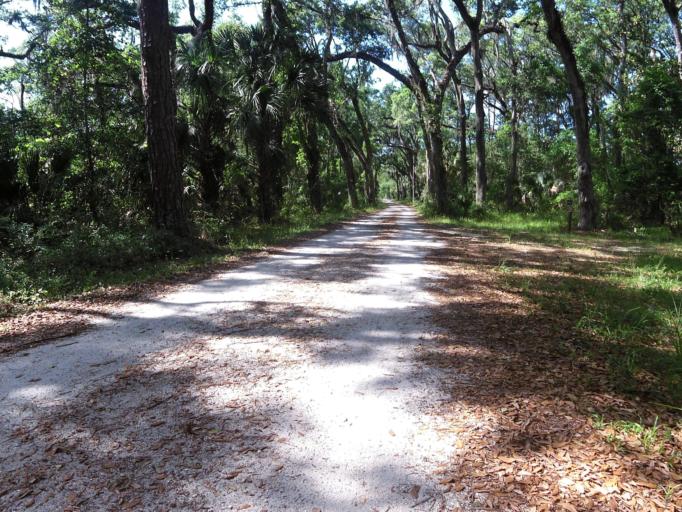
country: US
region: Florida
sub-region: Saint Johns County
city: Palm Valley
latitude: 30.1356
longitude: -81.3683
